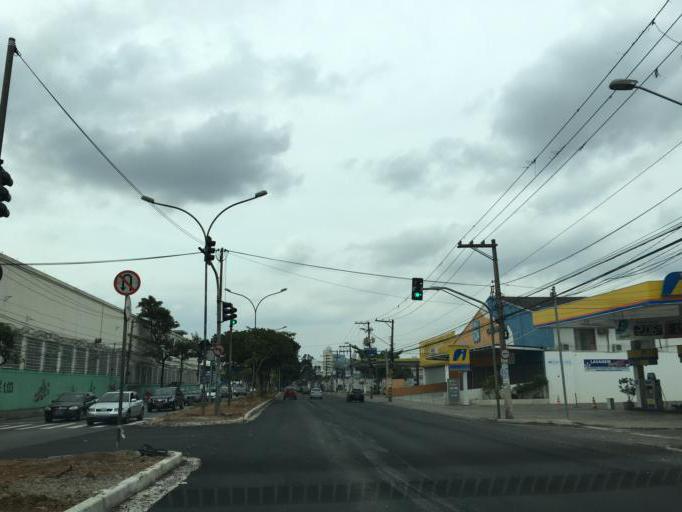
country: BR
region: Sao Paulo
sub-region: Osasco
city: Osasco
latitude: -23.5521
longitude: -46.7412
